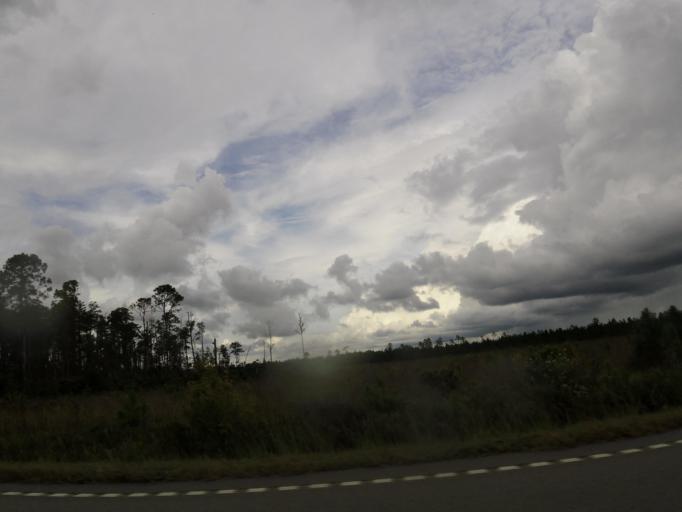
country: US
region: Florida
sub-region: Baker County
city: Macclenny
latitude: 30.5236
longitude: -82.1570
